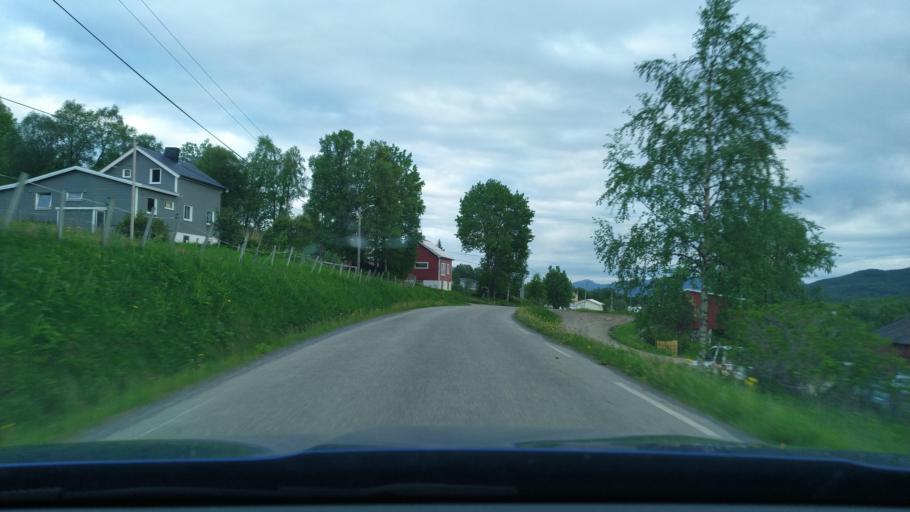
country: NO
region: Troms
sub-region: Tranoy
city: Vangsvika
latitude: 69.1142
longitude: 17.7940
